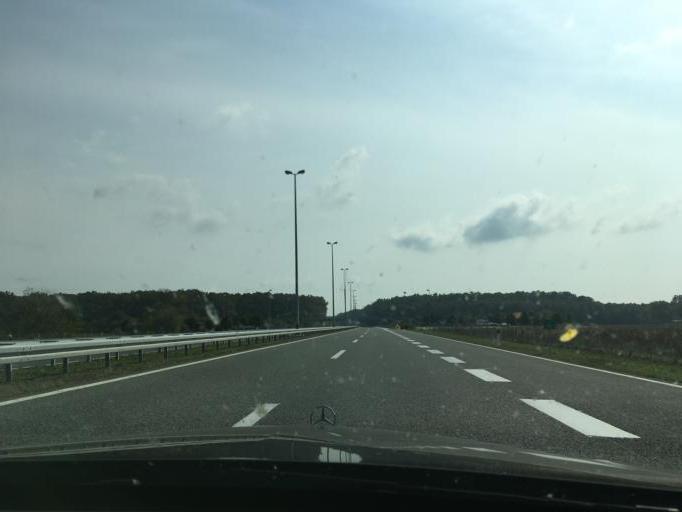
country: HR
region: Vukovarsko-Srijemska
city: Bosnjaci
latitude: 45.0584
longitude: 18.8098
